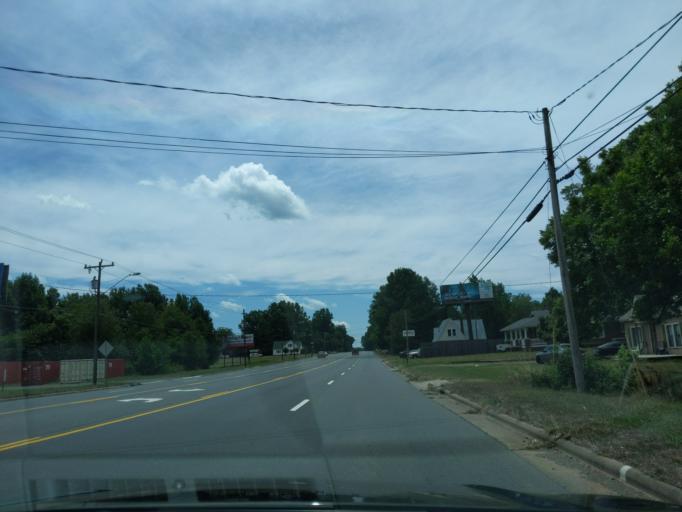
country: US
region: North Carolina
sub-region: Stanly County
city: Albemarle
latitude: 35.4242
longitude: -80.2119
